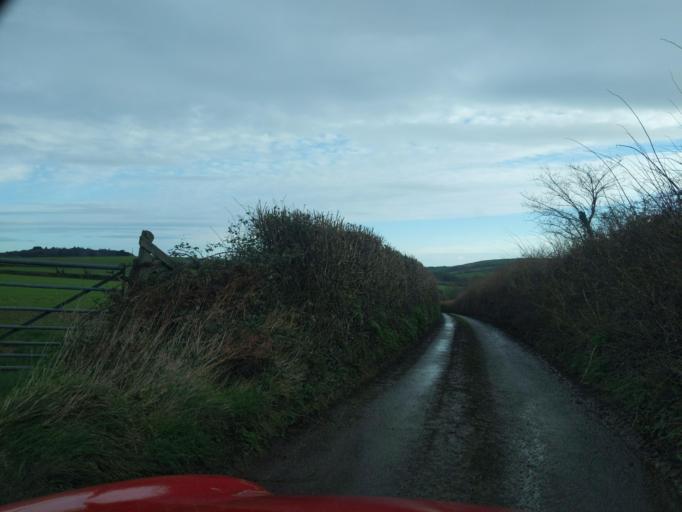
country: GB
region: England
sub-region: Devon
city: Salcombe
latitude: 50.2649
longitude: -3.6899
